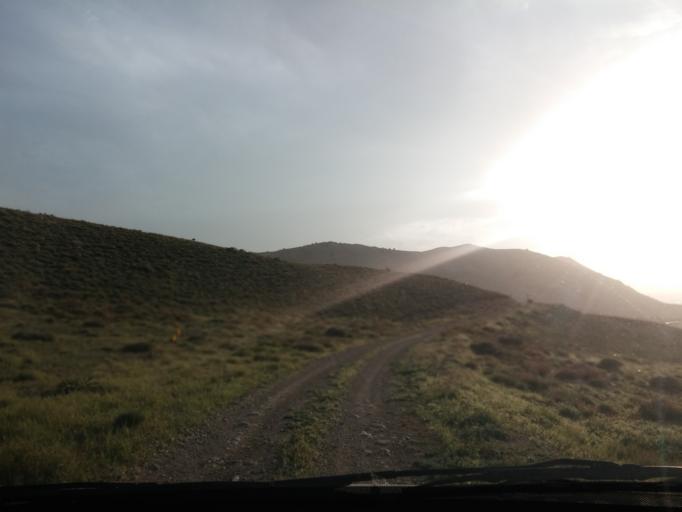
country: IR
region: Semnan
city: Istgah-e Rah Ahan-e Garmsar
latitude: 35.4886
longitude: 52.3020
